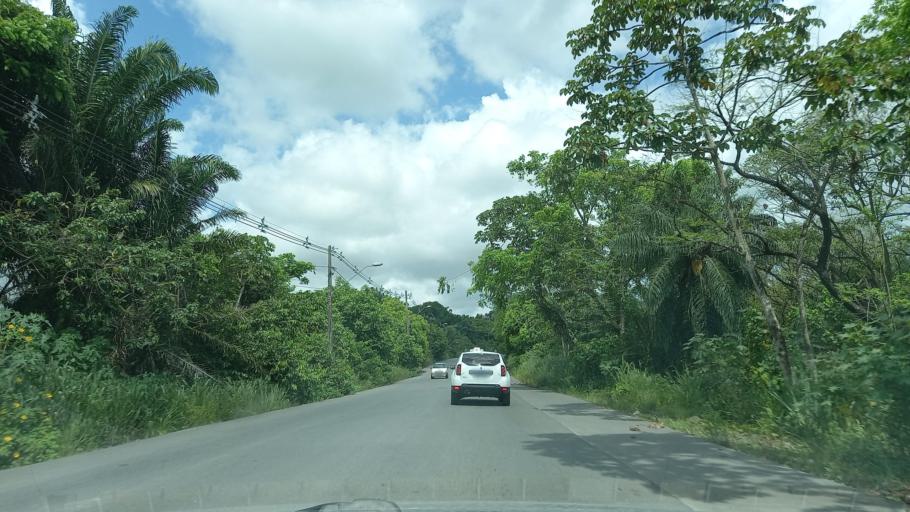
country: BR
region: Pernambuco
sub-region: Jaboatao Dos Guararapes
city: Jaboatao
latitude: -8.1576
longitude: -34.9965
